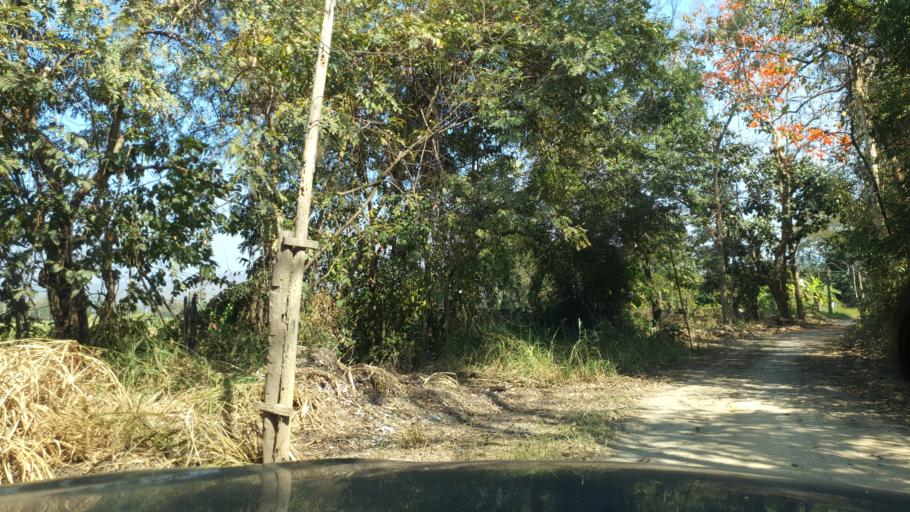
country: TH
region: Chiang Mai
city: San Kamphaeng
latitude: 18.7239
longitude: 99.1711
